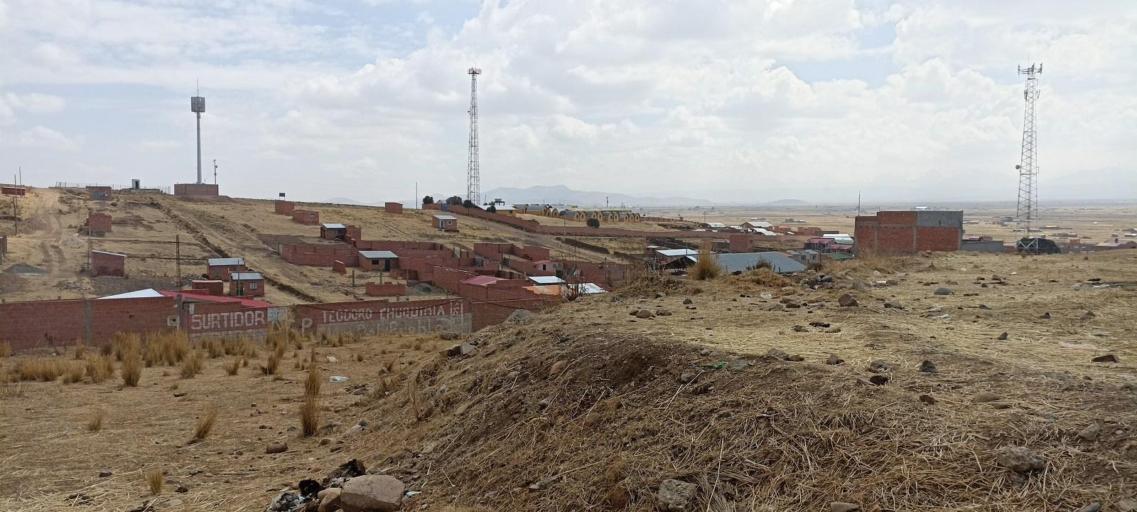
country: BO
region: La Paz
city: Batallas
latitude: -16.4014
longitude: -68.4804
